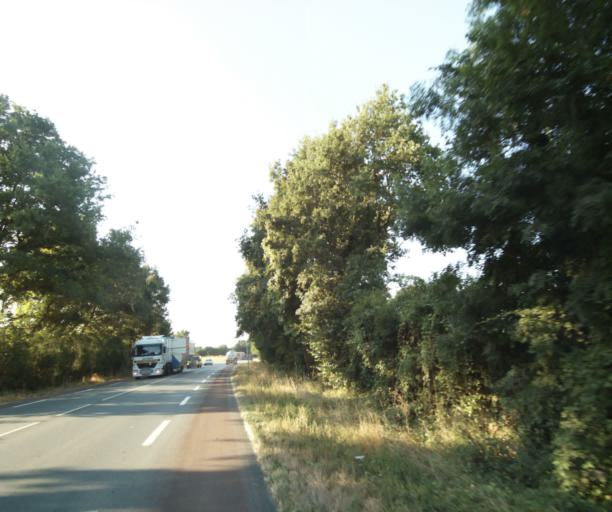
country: FR
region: Poitou-Charentes
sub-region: Departement de la Charente-Maritime
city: Cabariot
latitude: 45.9387
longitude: -0.8641
